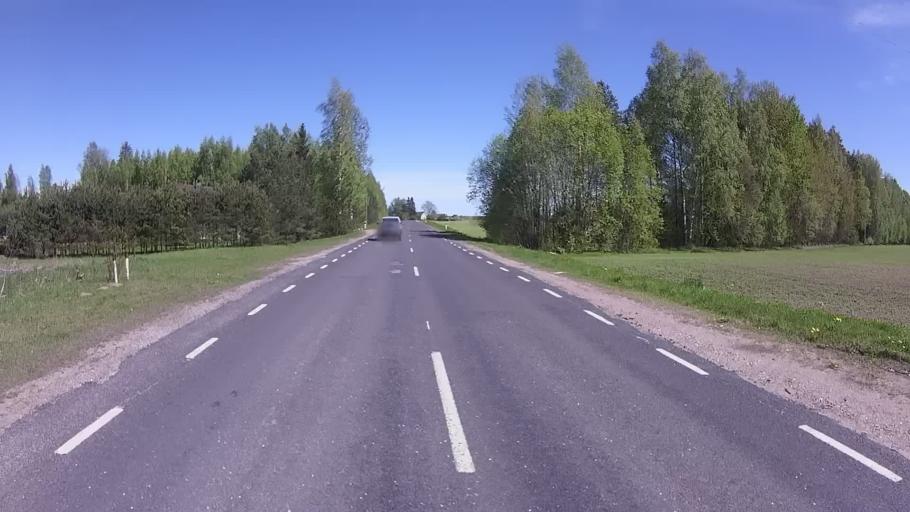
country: EE
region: Polvamaa
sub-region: Raepina vald
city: Rapina
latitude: 58.0302
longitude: 27.3854
